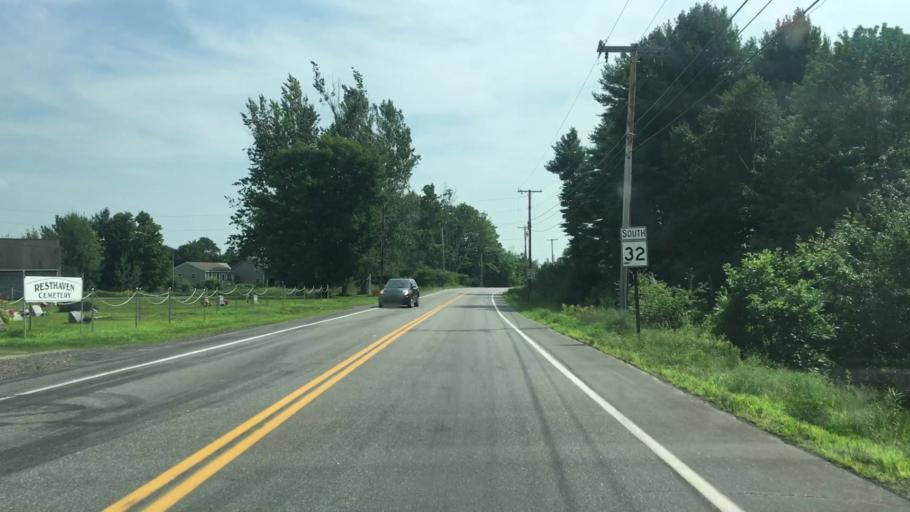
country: US
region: Maine
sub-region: Kennebec County
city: Windsor
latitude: 44.2942
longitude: -69.5854
